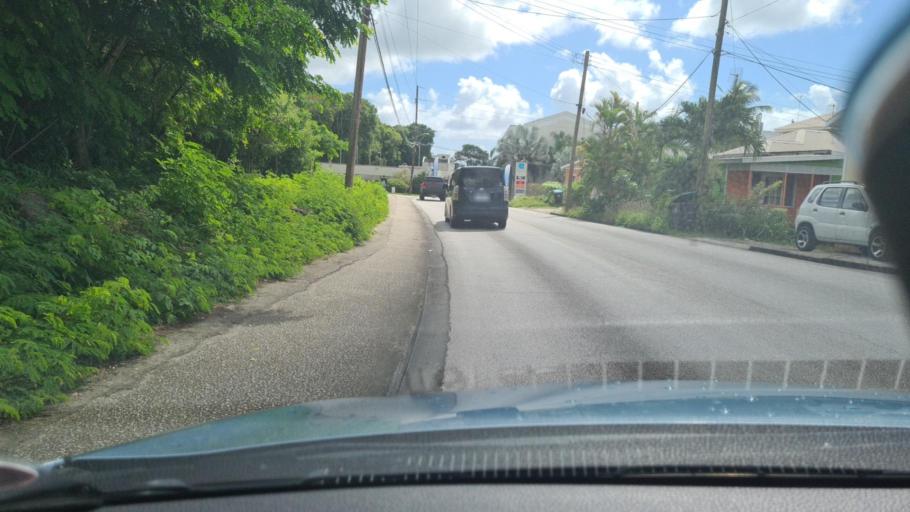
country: BB
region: Christ Church
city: Oistins
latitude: 13.0849
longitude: -59.5682
